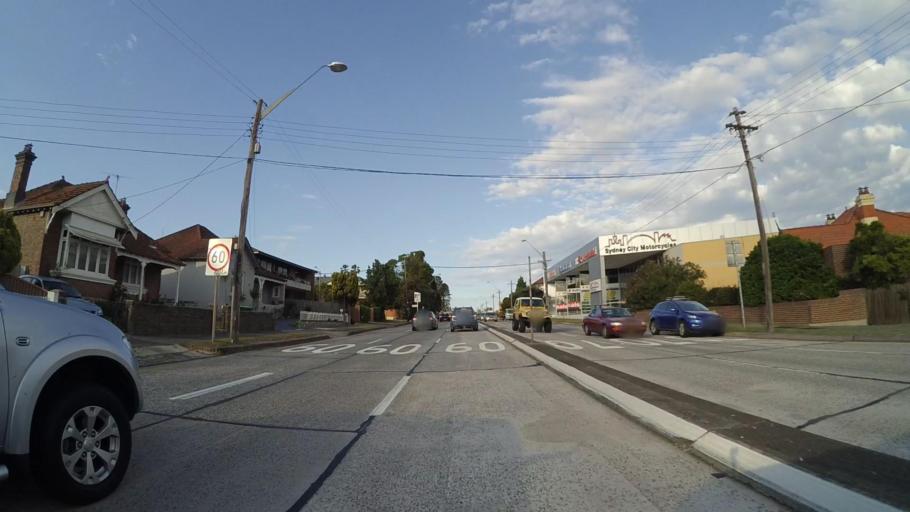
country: AU
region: New South Wales
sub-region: Kogarah
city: Beverly Park
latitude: -33.9714
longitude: 151.1327
